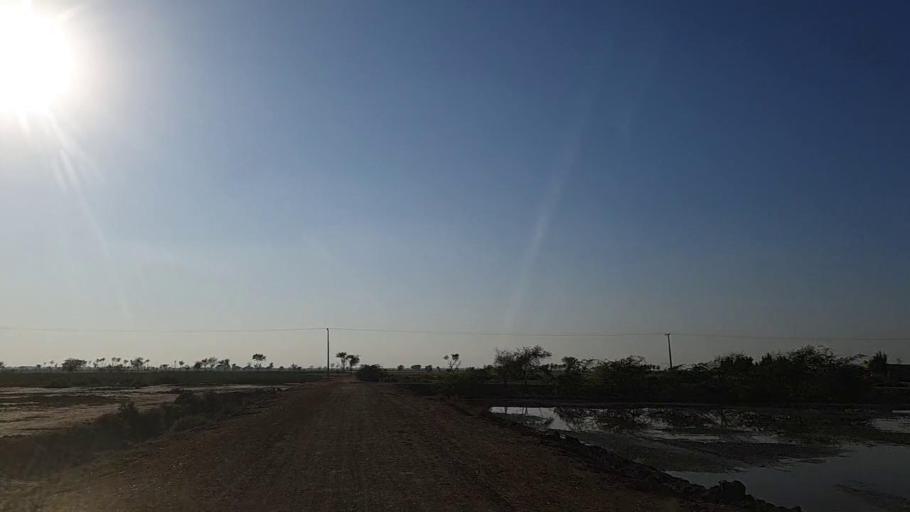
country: PK
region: Sindh
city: Samaro
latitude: 25.3486
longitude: 69.3651
